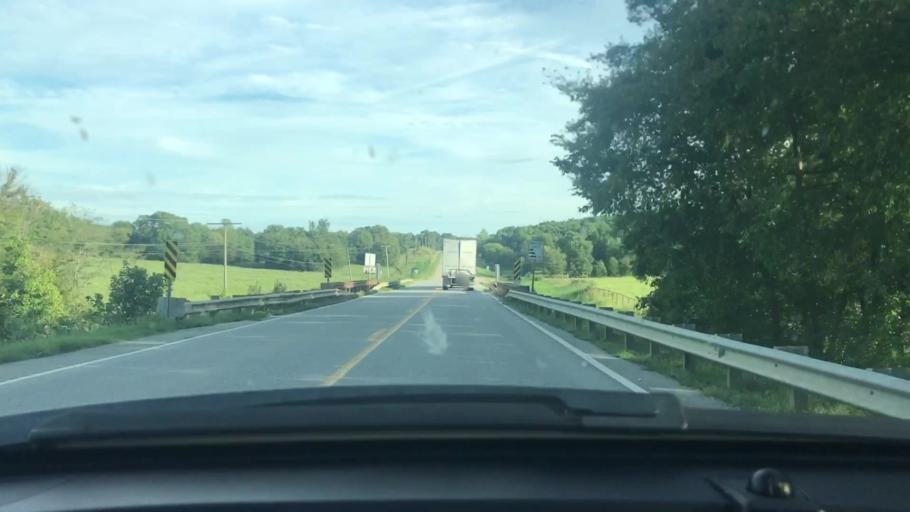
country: US
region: Arkansas
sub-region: Randolph County
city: Pocahontas
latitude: 36.1937
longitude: -91.1663
